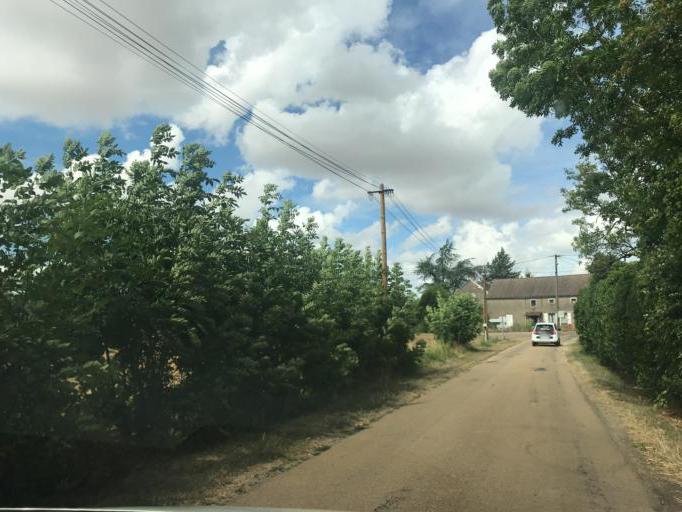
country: FR
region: Bourgogne
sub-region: Departement de l'Yonne
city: Fontenailles
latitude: 47.5659
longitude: 3.3423
